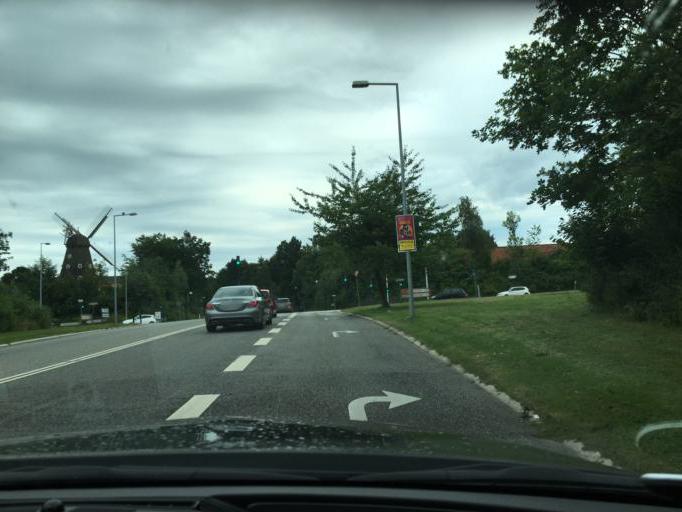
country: DK
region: Capital Region
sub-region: Horsholm Kommune
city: Horsholm
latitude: 55.8786
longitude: 12.4942
